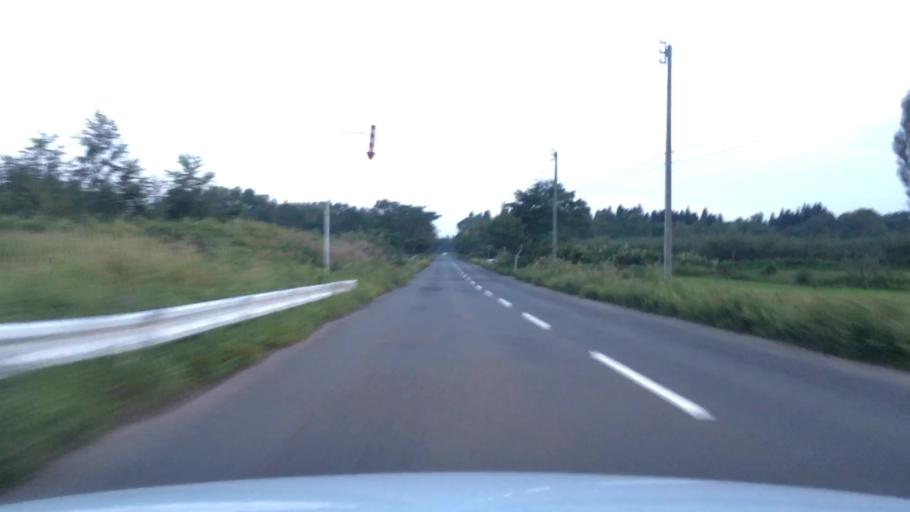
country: JP
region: Aomori
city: Shimokizukuri
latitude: 40.6850
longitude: 140.3695
